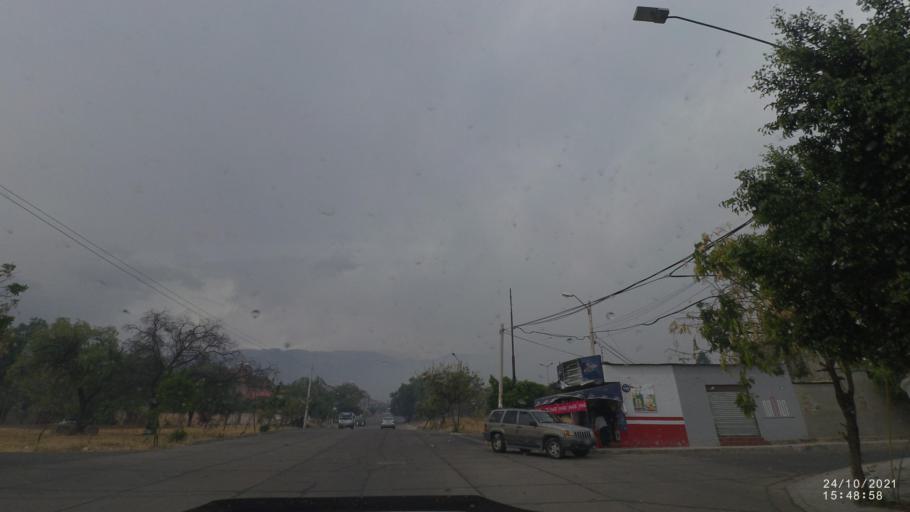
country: BO
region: Cochabamba
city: Cochabamba
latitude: -17.3624
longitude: -66.1549
